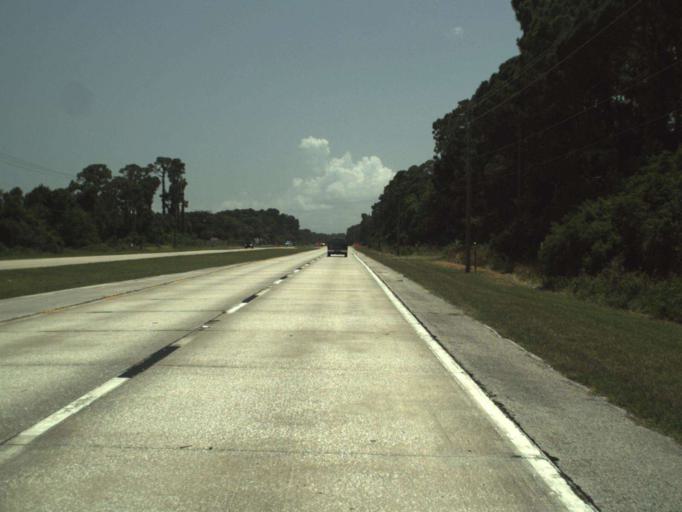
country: US
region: Florida
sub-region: Volusia County
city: Oak Hill
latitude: 28.9252
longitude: -80.8743
